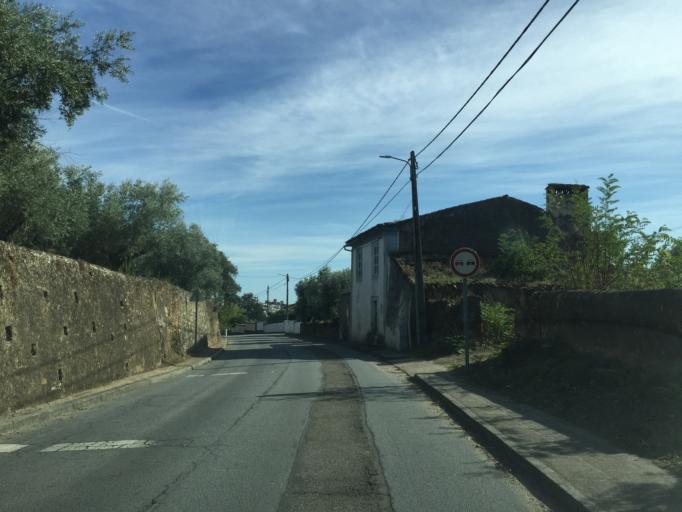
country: PT
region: Portalegre
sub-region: Portalegre
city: Portalegre
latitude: 39.3081
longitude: -7.4388
